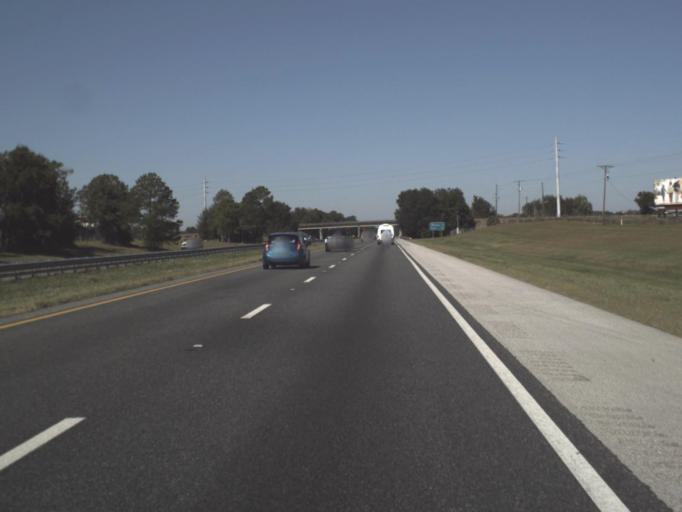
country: US
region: Florida
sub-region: Sumter County
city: Wildwood
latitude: 28.7969
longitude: -81.9961
